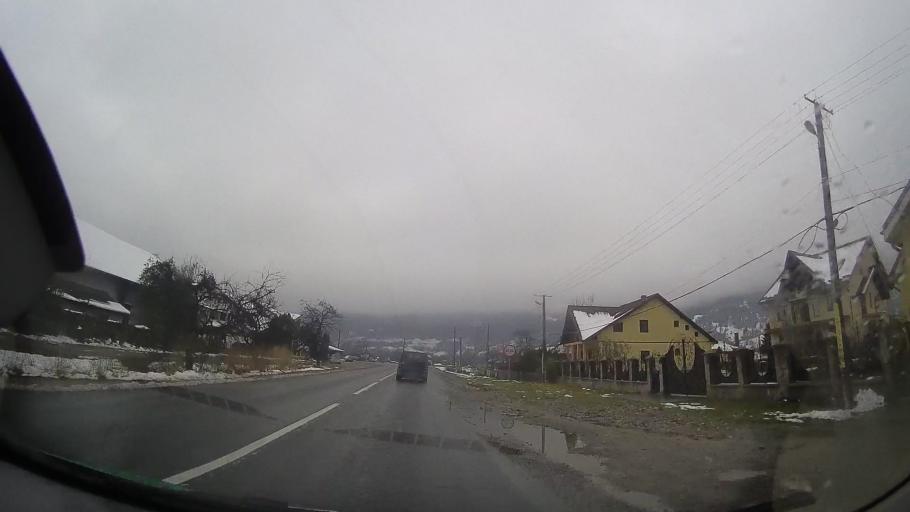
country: RO
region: Neamt
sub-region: Comuna Pangarati
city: Stejaru
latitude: 46.9113
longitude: 26.1803
